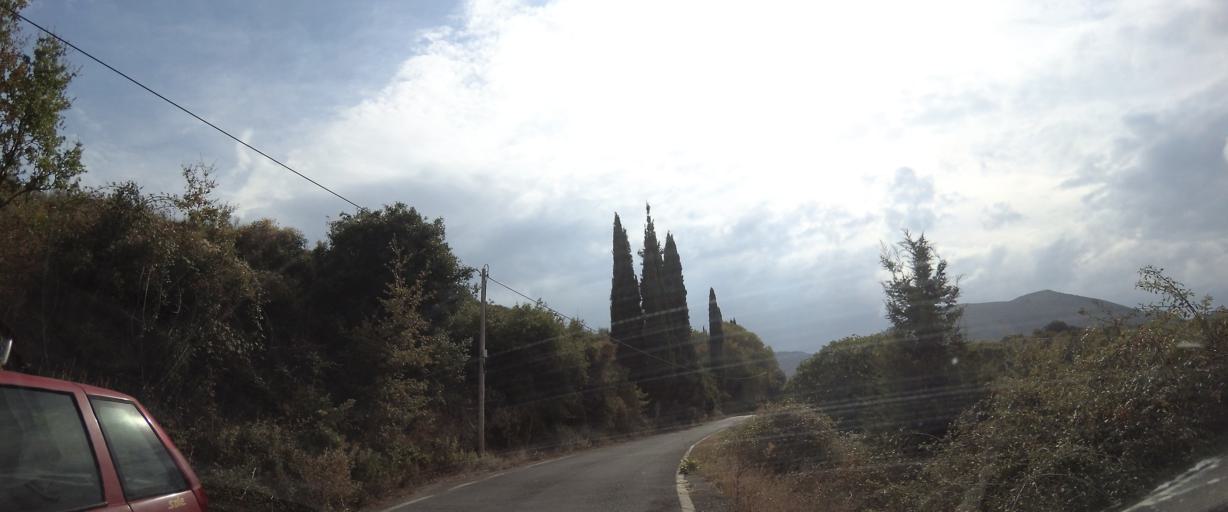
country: GR
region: Ionian Islands
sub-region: Nomos Kerkyras
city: Acharavi
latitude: 39.7690
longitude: 19.8808
